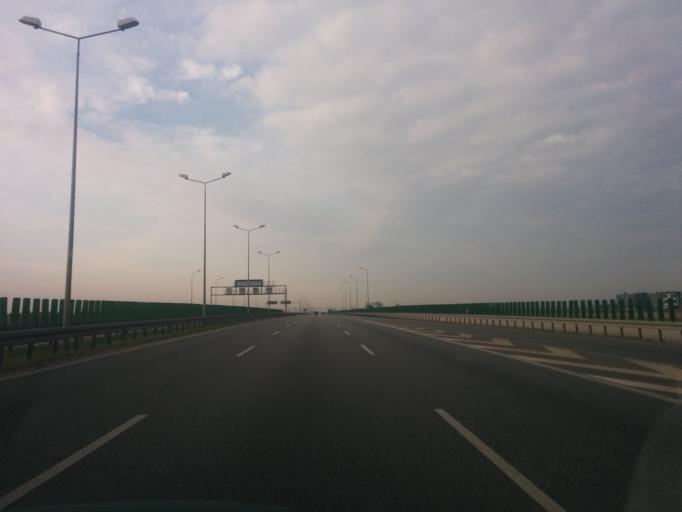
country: PL
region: Masovian Voivodeship
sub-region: Warszawa
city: Bemowo
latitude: 52.2384
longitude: 20.8869
